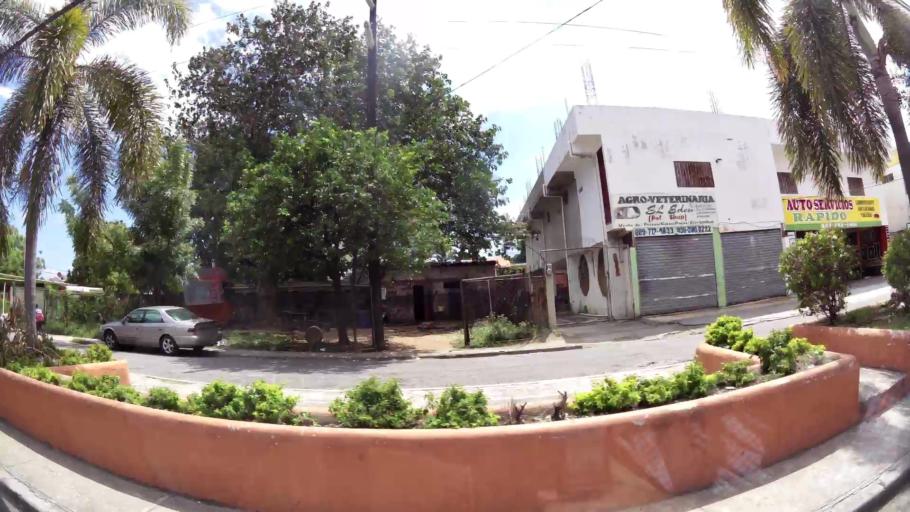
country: DO
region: San Cristobal
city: San Cristobal
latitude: 18.4150
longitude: -70.0998
